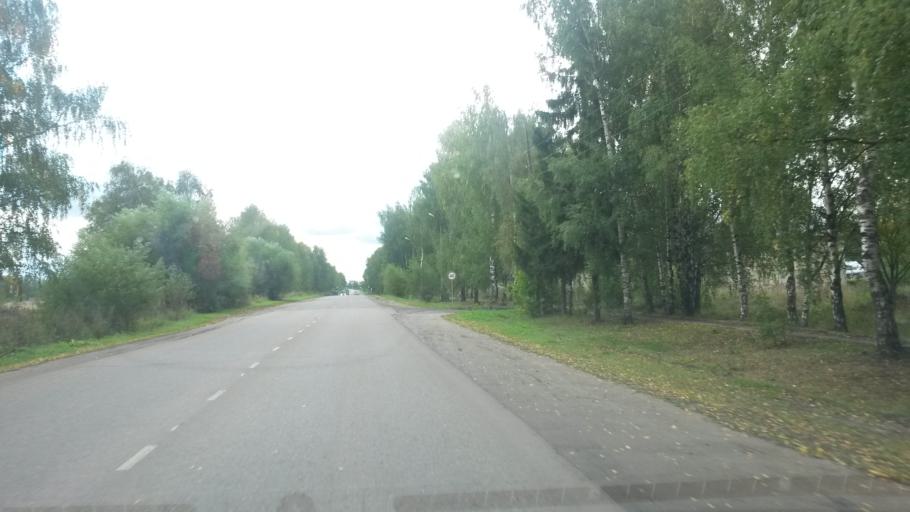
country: RU
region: Ivanovo
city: Zavolzhsk
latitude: 57.4741
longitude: 42.1555
